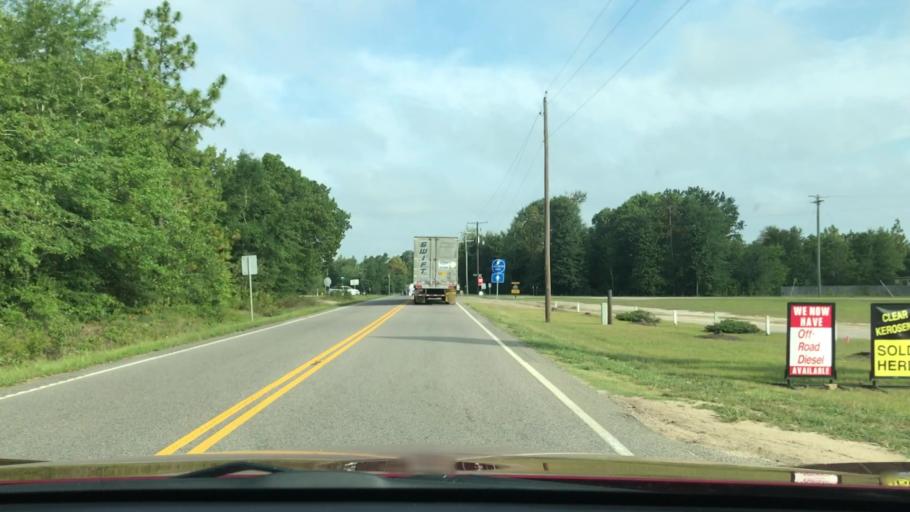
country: US
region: South Carolina
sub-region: Barnwell County
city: Williston
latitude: 33.6284
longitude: -81.3018
